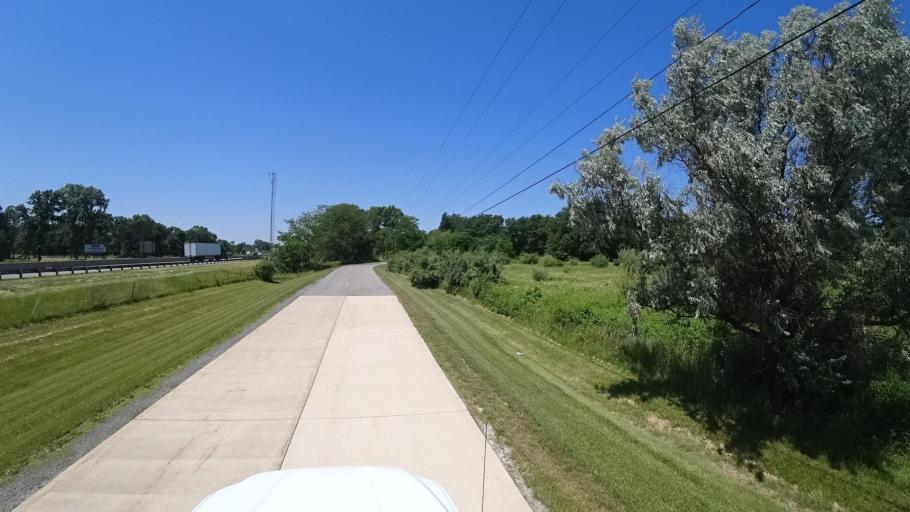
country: US
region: Indiana
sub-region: Porter County
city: Burns Harbor
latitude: 41.6070
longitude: -87.1325
